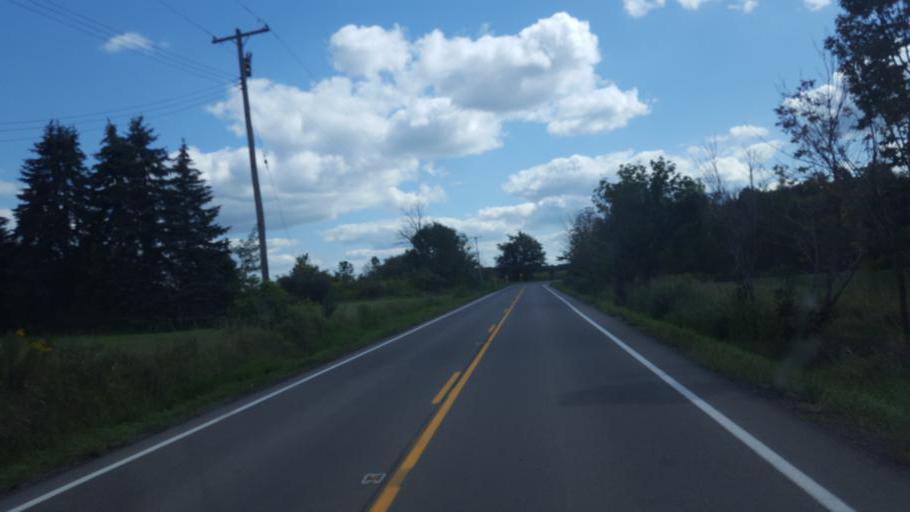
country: US
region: Ohio
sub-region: Wayne County
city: West Salem
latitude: 40.9825
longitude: -82.2163
